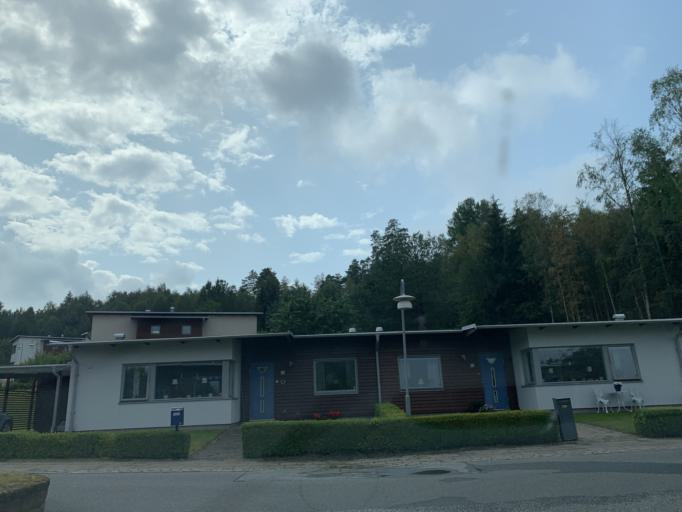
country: SE
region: Vaestra Goetaland
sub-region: Goteborg
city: Eriksbo
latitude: 57.7452
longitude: 12.0383
